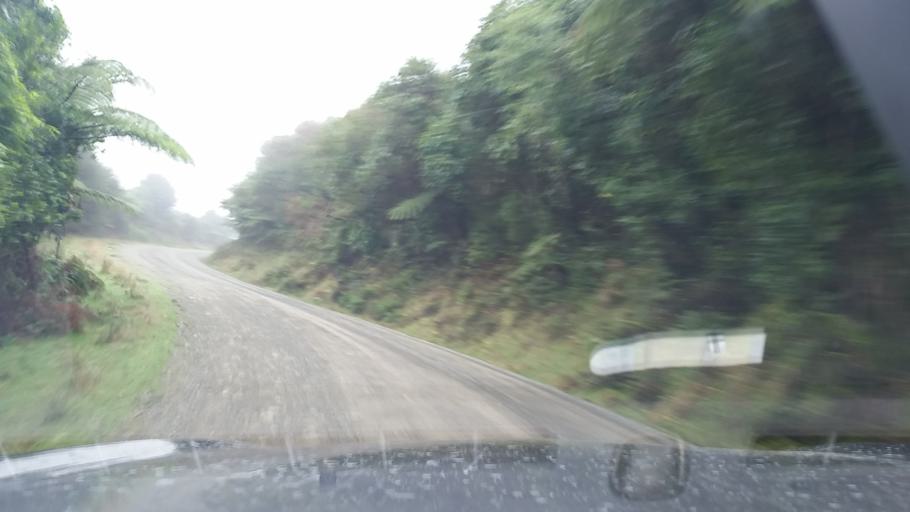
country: NZ
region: Marlborough
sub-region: Marlborough District
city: Picton
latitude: -41.1783
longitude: 173.9851
